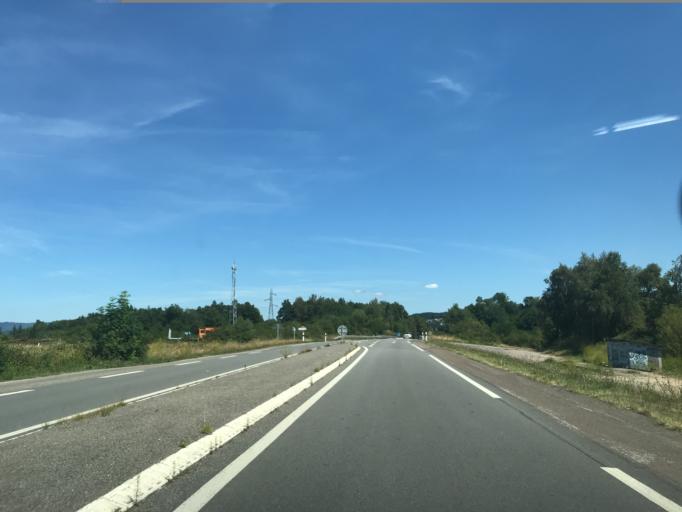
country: FR
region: Limousin
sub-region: Departement de la Correze
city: Naves
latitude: 45.3049
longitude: 1.8178
